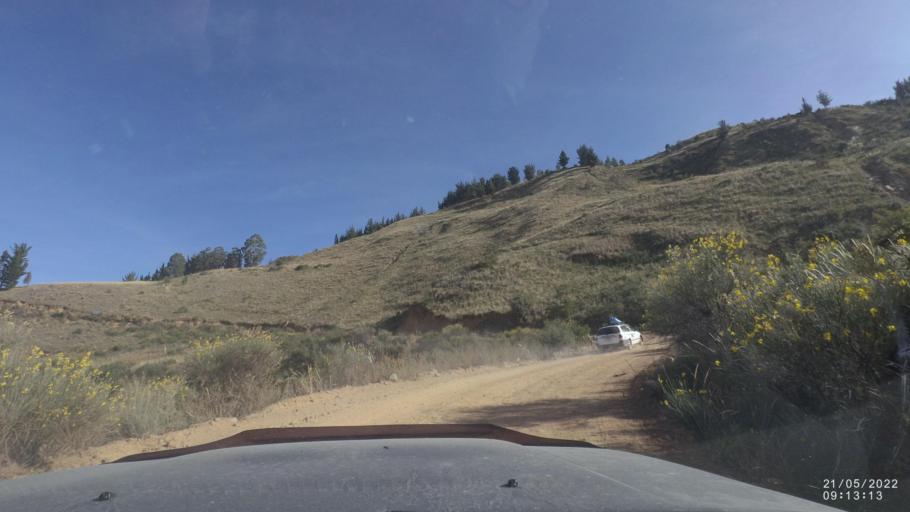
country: BO
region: Cochabamba
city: Cochabamba
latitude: -17.3666
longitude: -66.0254
